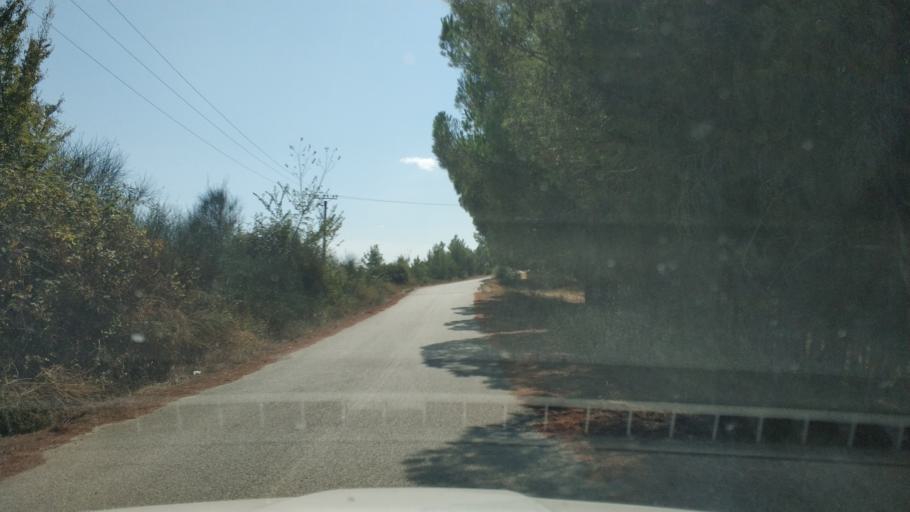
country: AL
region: Fier
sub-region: Rrethi i Lushnjes
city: Kolonje
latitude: 40.8214
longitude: 19.5948
